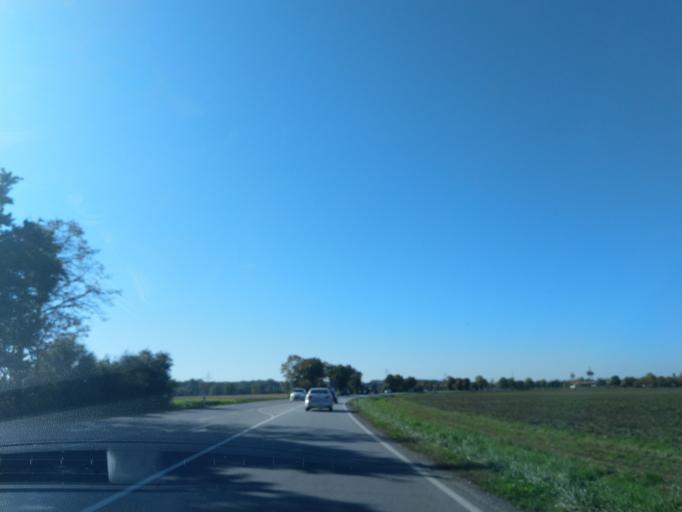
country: DE
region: Bavaria
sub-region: Lower Bavaria
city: Plattling
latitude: 48.7931
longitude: 12.9044
